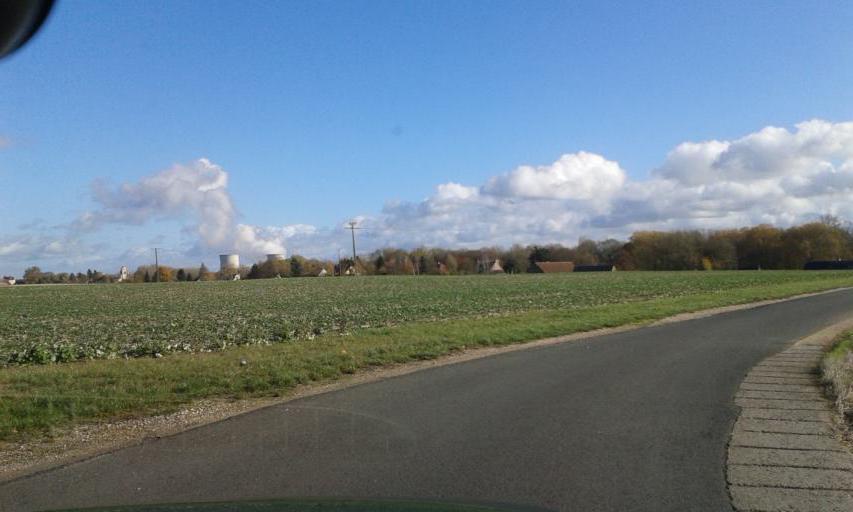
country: FR
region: Centre
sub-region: Departement du Loir-et-Cher
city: Mer
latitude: 47.7042
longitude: 1.5250
